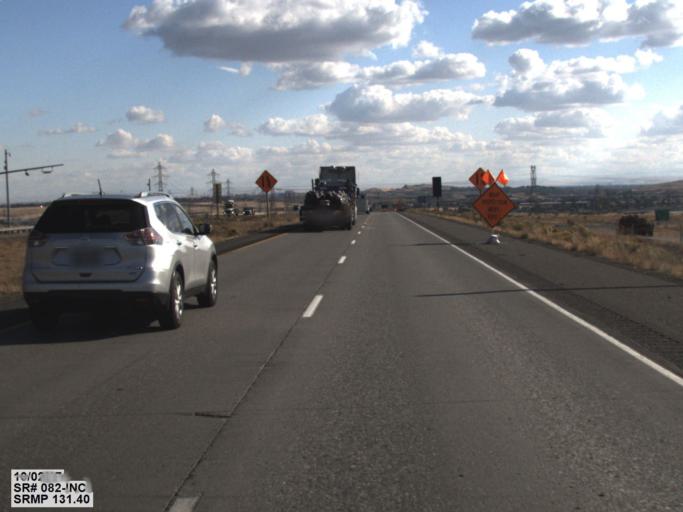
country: US
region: Oregon
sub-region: Umatilla County
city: Umatilla
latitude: 45.9480
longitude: -119.3366
